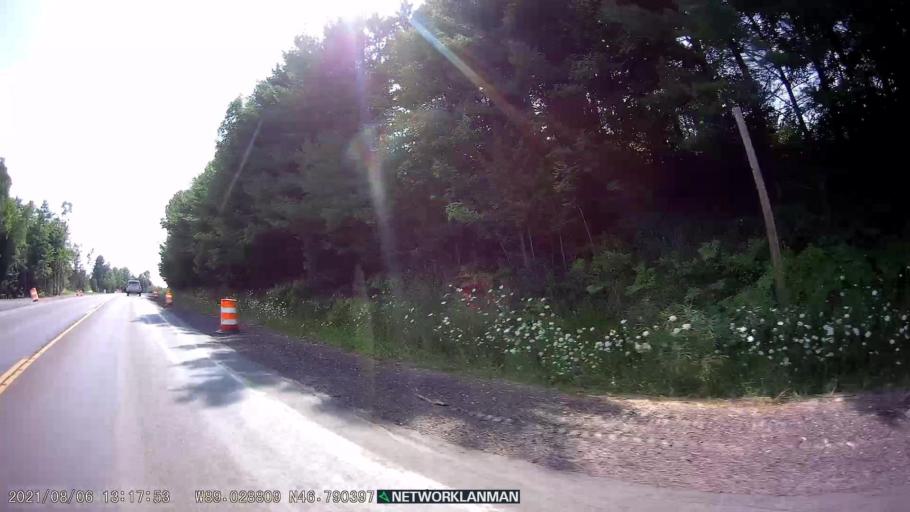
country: US
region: Michigan
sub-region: Ontonagon County
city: Ontonagon
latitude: 46.7900
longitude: -89.0291
